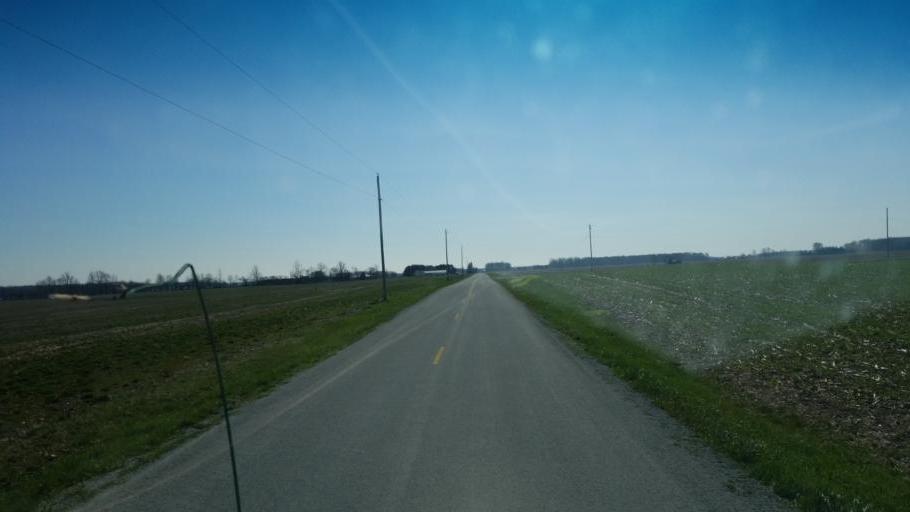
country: US
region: Ohio
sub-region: Hardin County
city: Kenton
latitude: 40.7020
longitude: -83.5490
